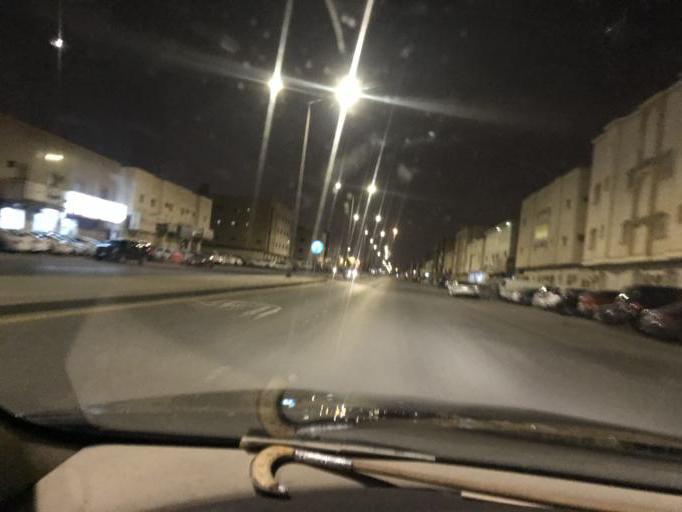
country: SA
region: Ar Riyad
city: Riyadh
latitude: 24.7956
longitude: 46.7036
